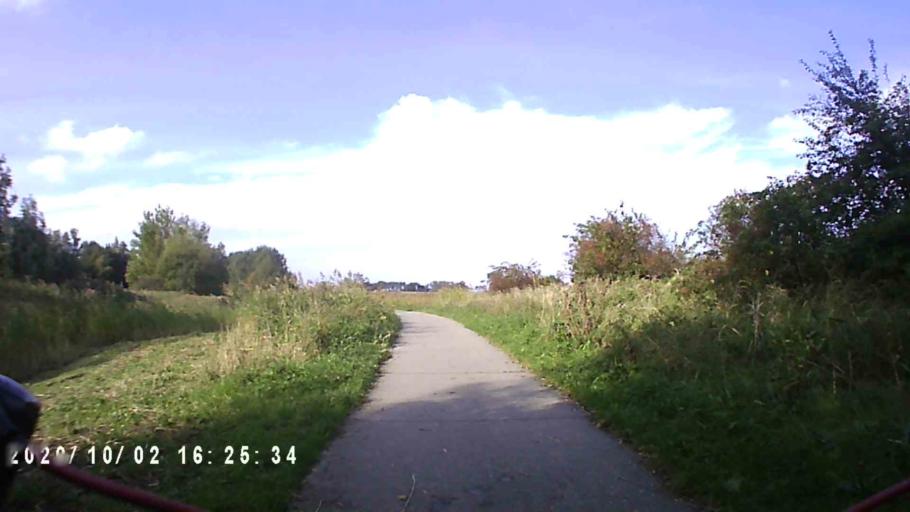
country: NL
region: Groningen
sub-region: Gemeente Zuidhorn
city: Grijpskerk
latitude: 53.2837
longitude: 6.3136
